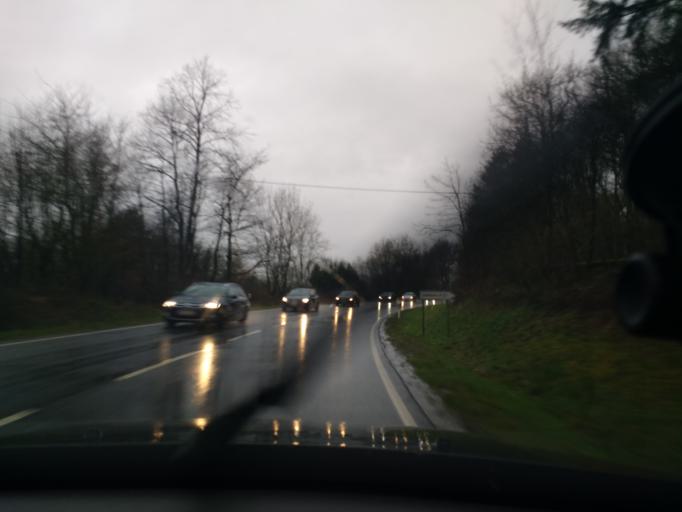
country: DE
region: Rheinland-Pfalz
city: Wiltingen
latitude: 49.7034
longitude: 6.6293
